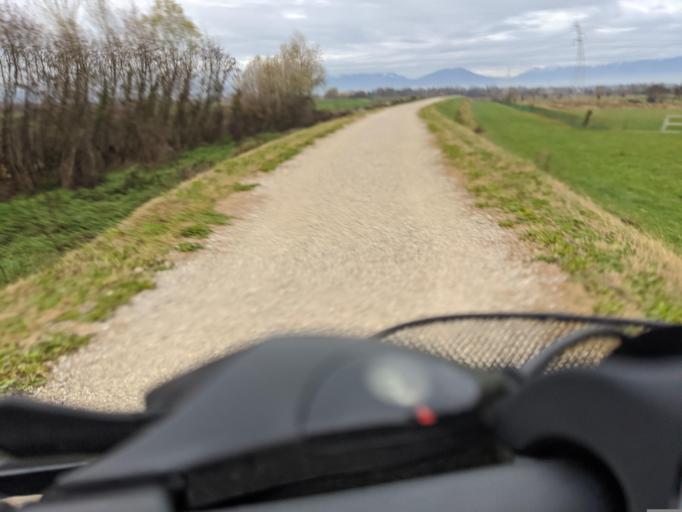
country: IT
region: Veneto
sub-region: Provincia di Vicenza
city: Dueville
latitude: 45.6123
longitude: 11.5408
